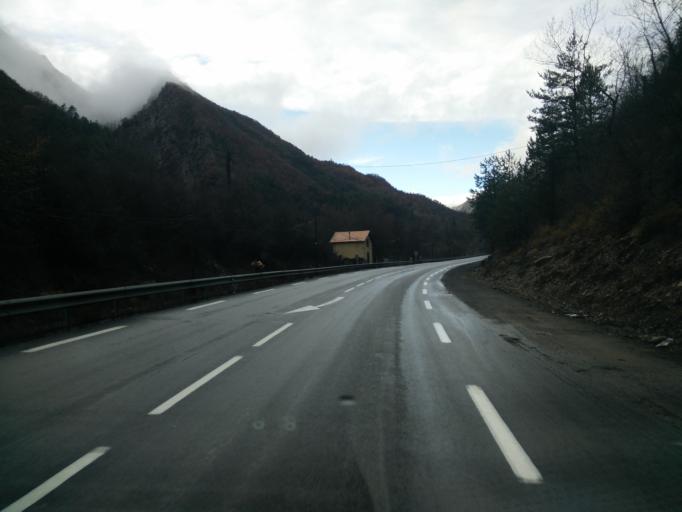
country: FR
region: Provence-Alpes-Cote d'Azur
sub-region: Departement des Alpes-Maritimes
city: Gilette
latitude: 43.9287
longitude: 7.0952
